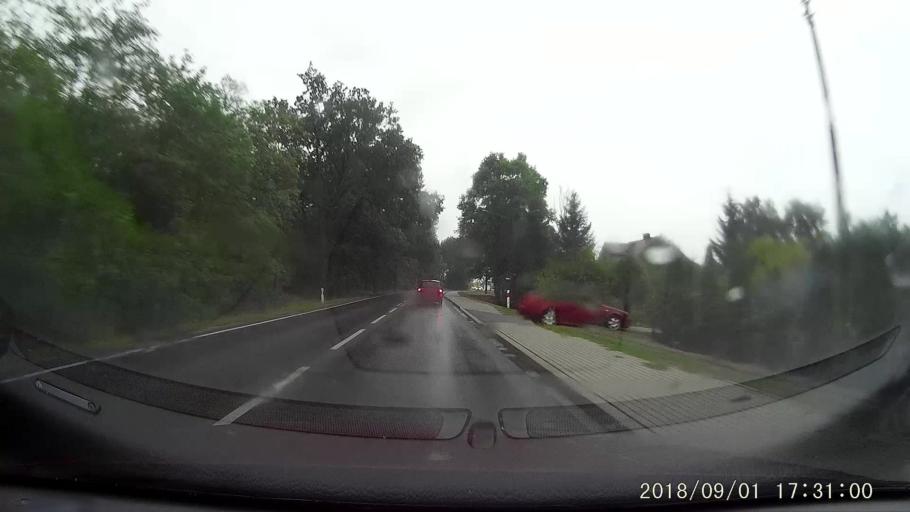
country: PL
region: Lubusz
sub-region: Powiat zaganski
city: Zagan
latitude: 51.6365
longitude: 15.3242
